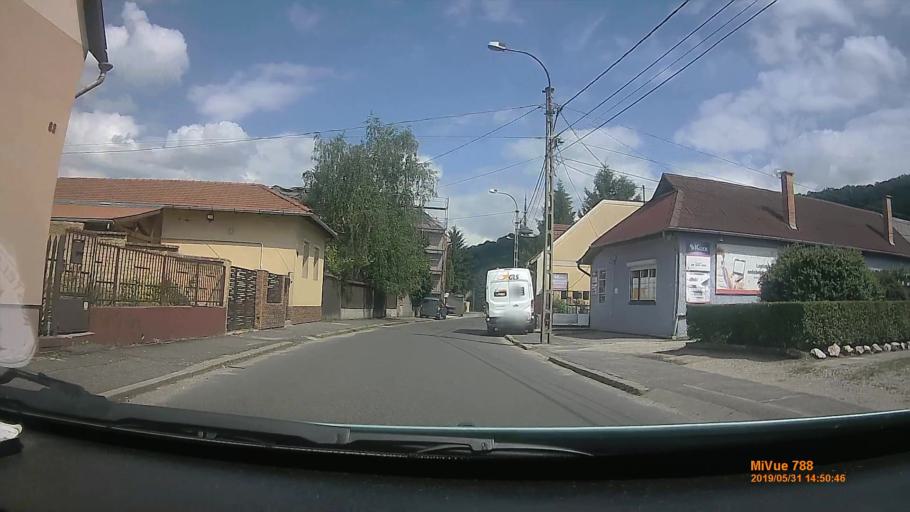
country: HU
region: Borsod-Abauj-Zemplen
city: Miskolc
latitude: 48.1014
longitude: 20.7658
